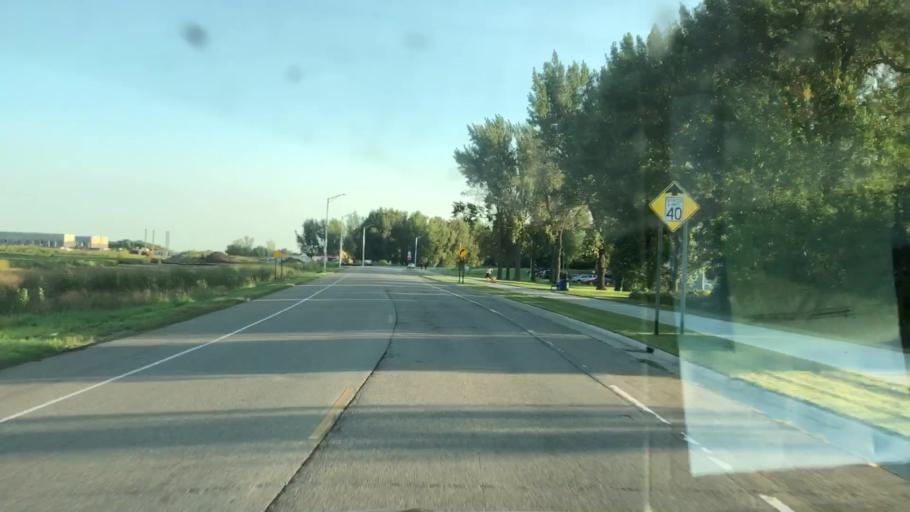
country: US
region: Minnesota
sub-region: Nobles County
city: Worthington
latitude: 43.6206
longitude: -95.6335
